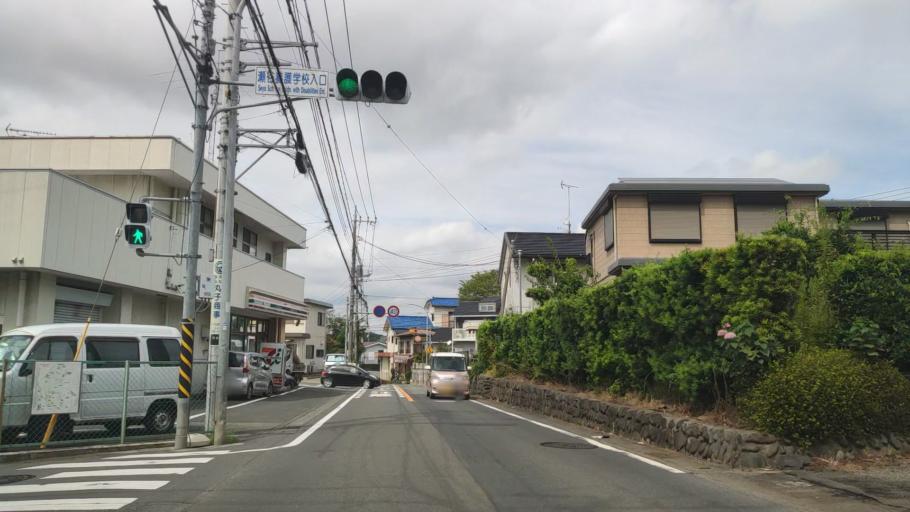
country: JP
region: Kanagawa
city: Minami-rinkan
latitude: 35.4858
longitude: 139.4738
